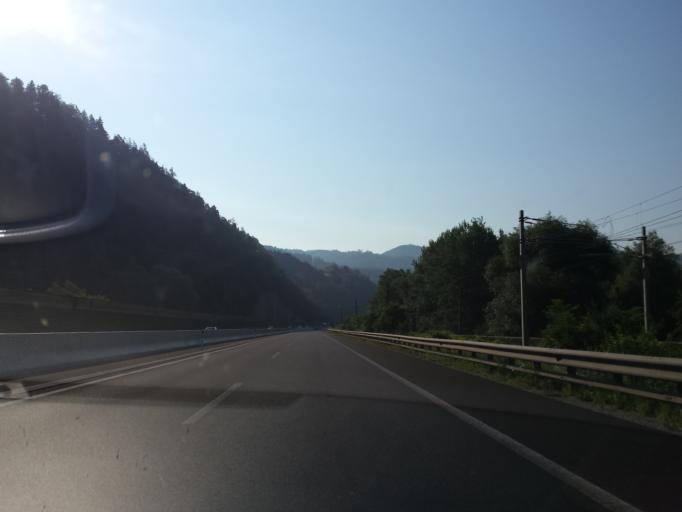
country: AT
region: Styria
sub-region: Politischer Bezirk Graz-Umgebung
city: Frohnleiten
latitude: 47.2370
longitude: 15.3274
